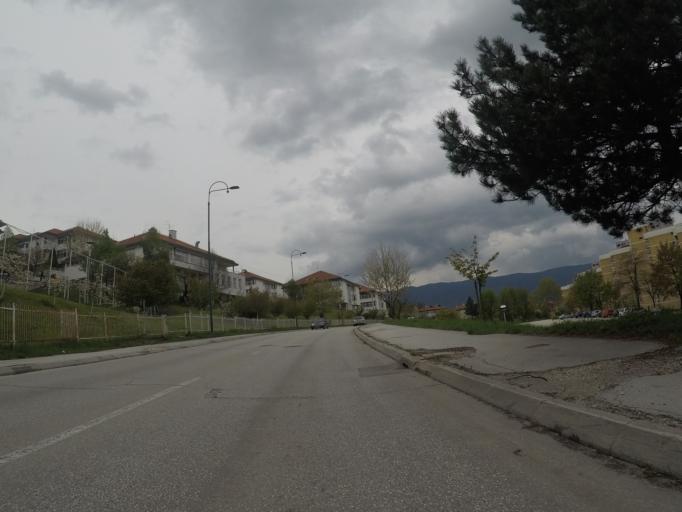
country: BA
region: Federation of Bosnia and Herzegovina
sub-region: Kanton Sarajevo
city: Sarajevo
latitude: 43.8382
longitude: 18.3490
